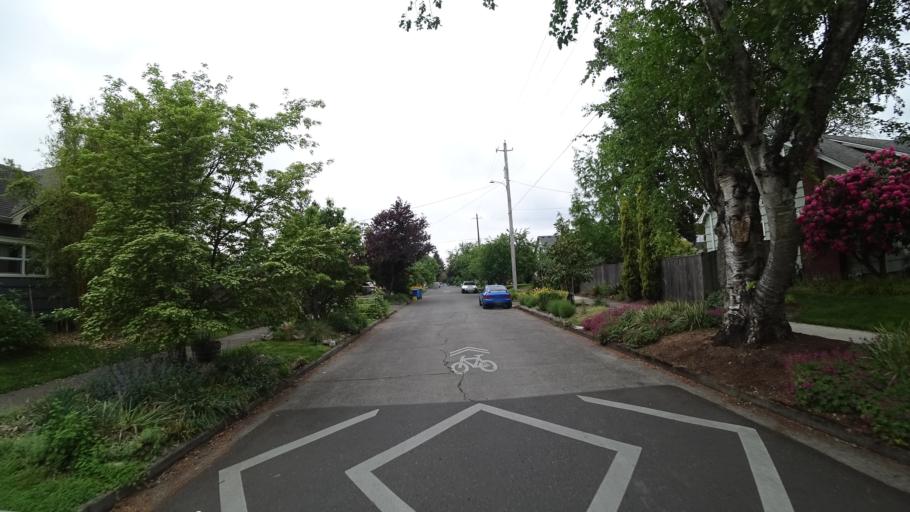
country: US
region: Oregon
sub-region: Multnomah County
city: Portland
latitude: 45.5469
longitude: -122.6078
